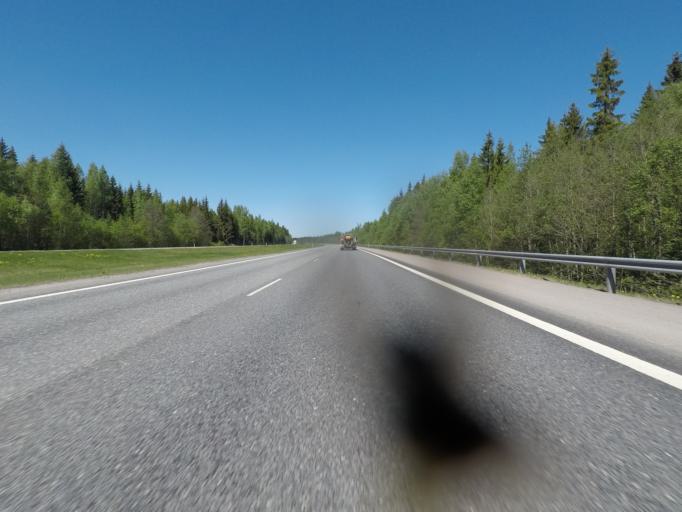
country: FI
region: Haeme
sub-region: Haemeenlinna
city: Haemeenlinna
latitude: 60.9455
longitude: 24.5084
